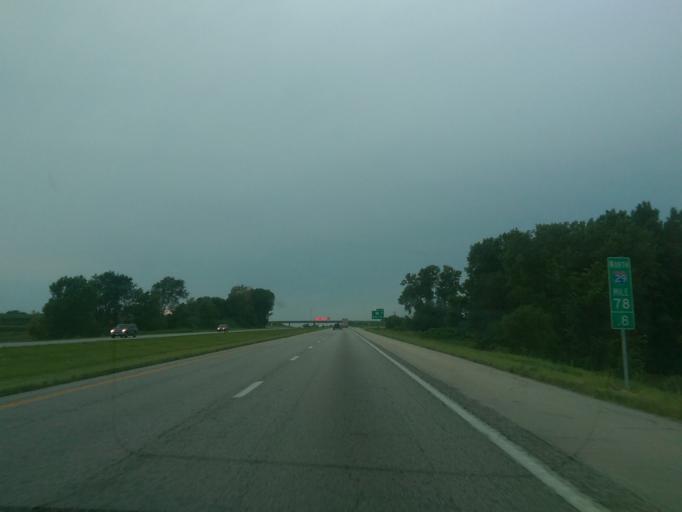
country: US
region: Missouri
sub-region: Holt County
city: Mound City
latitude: 40.0711
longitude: -95.1860
